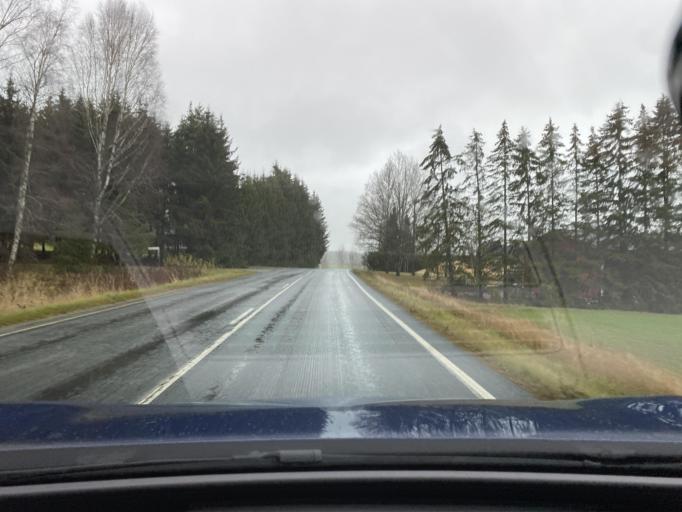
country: FI
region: Varsinais-Suomi
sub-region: Loimaa
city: Alastaro
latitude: 60.9366
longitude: 22.8683
